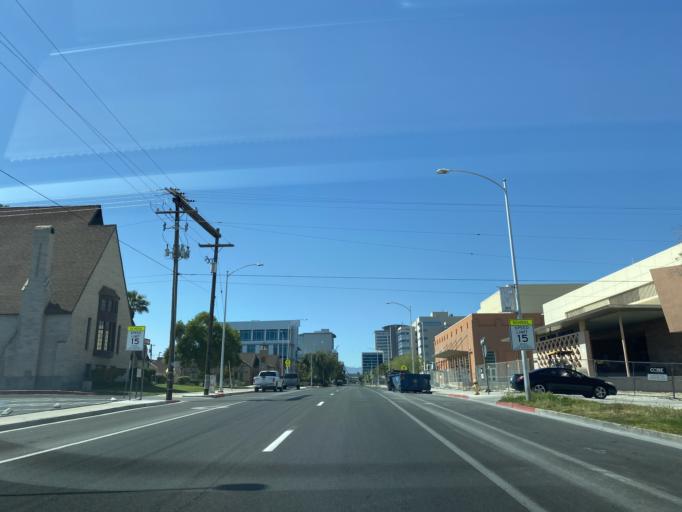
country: US
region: Nevada
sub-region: Clark County
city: Las Vegas
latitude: 36.1622
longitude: -115.1382
